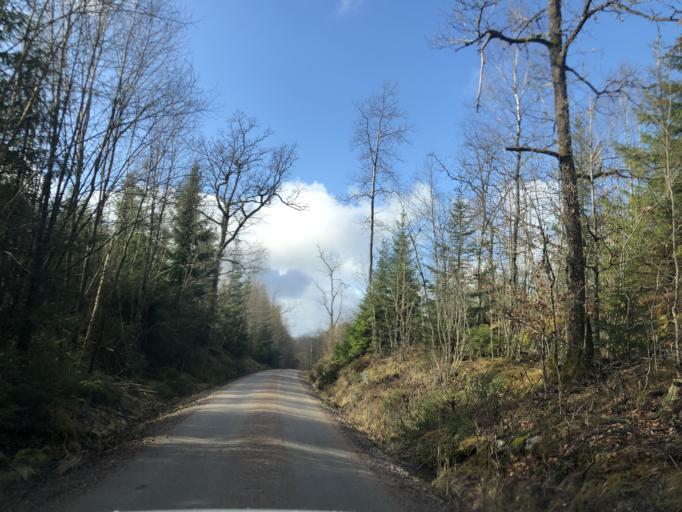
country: SE
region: Vaestra Goetaland
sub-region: Boras Kommun
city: Dalsjofors
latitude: 57.8274
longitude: 13.2029
